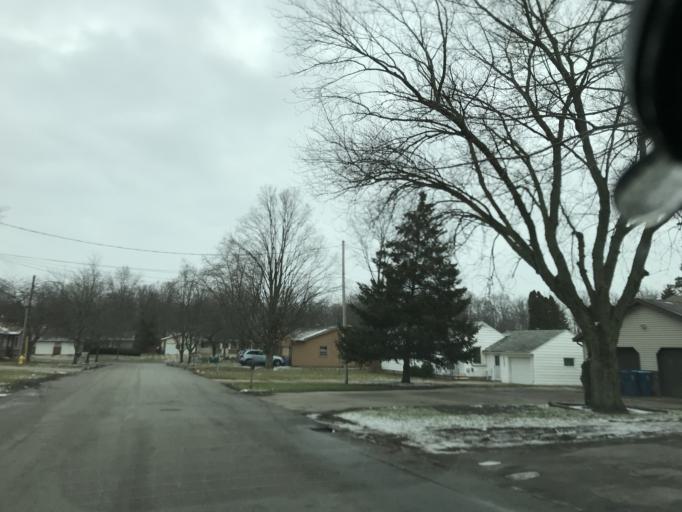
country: US
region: Michigan
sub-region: Kent County
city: East Grand Rapids
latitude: 42.9163
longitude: -85.5940
